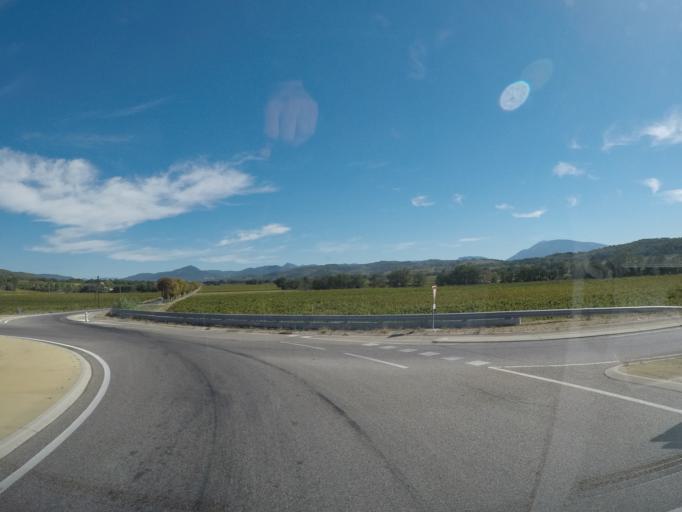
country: FR
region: Provence-Alpes-Cote d'Azur
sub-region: Departement du Vaucluse
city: Visan
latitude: 44.2913
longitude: 4.9879
